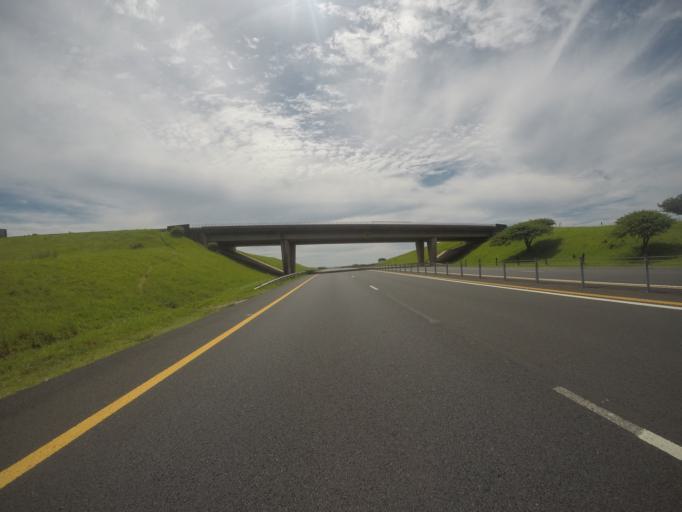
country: ZA
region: KwaZulu-Natal
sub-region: iLembe District Municipality
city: Mandeni
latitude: -29.1845
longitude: 31.4822
